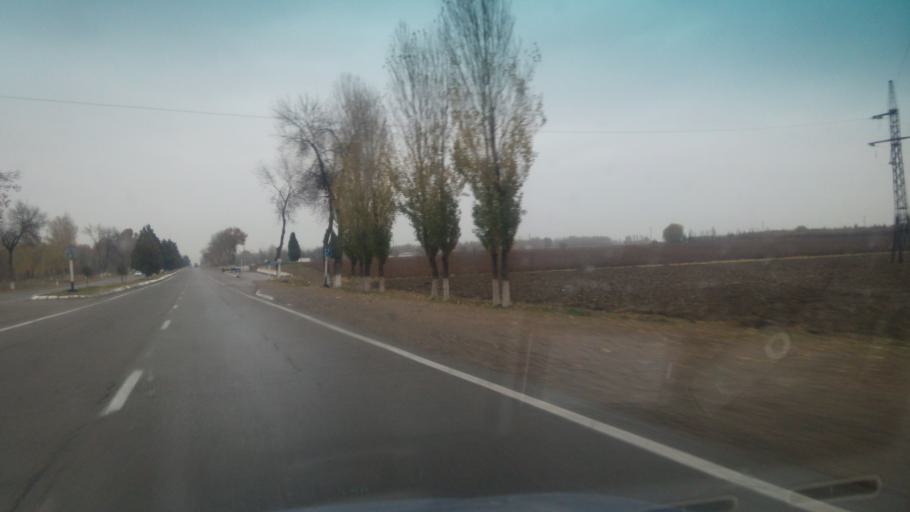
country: UZ
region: Toshkent
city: Zafar
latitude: 41.0345
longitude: 68.8727
